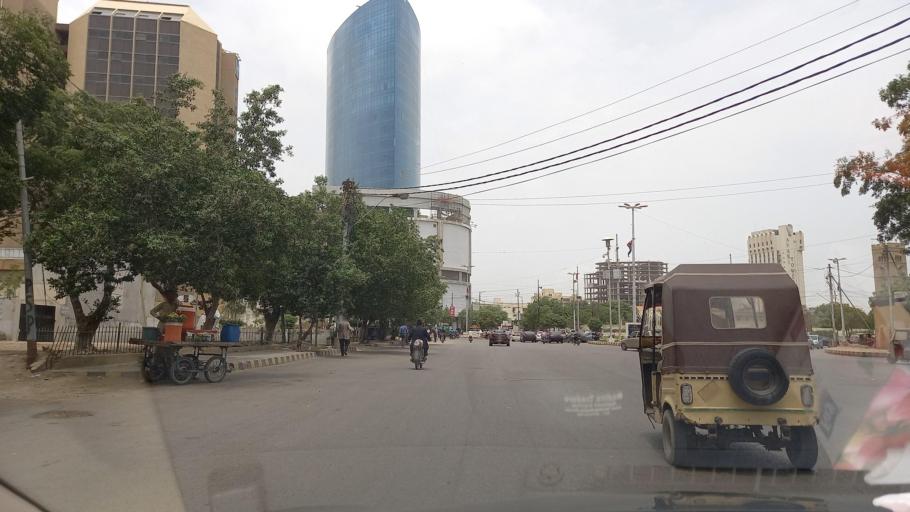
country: PK
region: Sindh
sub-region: Karachi District
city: Karachi
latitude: 24.8541
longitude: 67.0271
